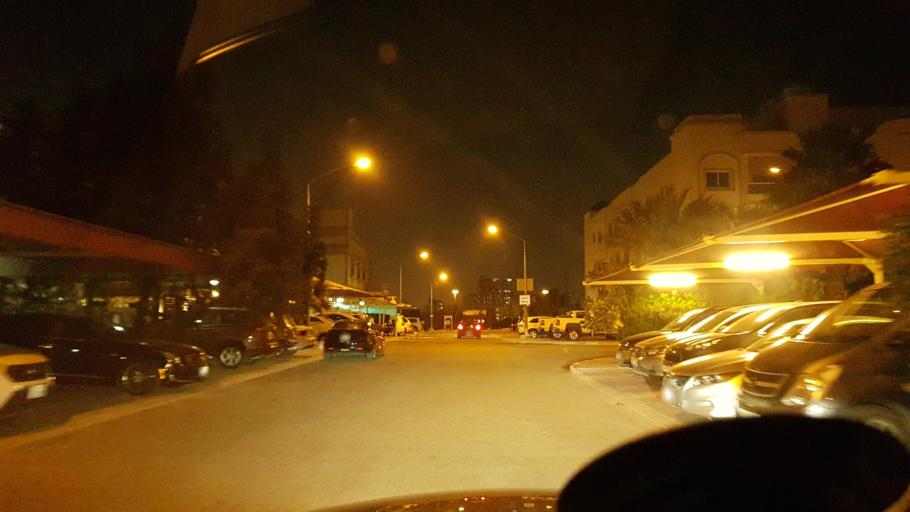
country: KW
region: Al Ahmadi
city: Al Manqaf
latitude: 29.1167
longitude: 48.1267
